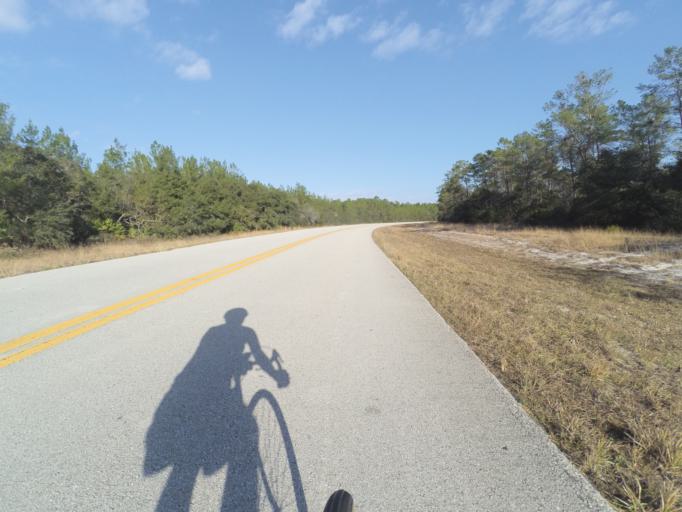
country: US
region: Florida
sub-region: Lake County
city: Astor
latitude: 29.1257
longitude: -81.5785
